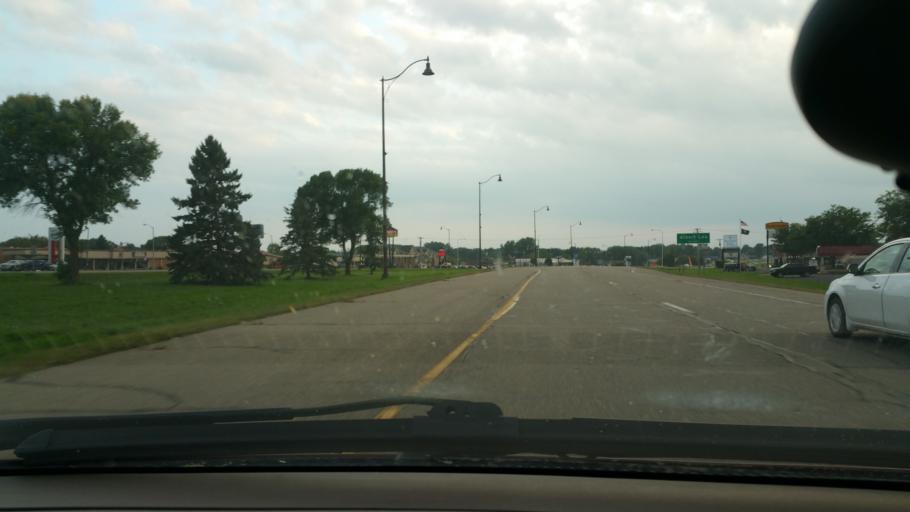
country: US
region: Minnesota
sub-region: Freeborn County
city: Albert Lea
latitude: 43.6573
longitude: -93.3349
